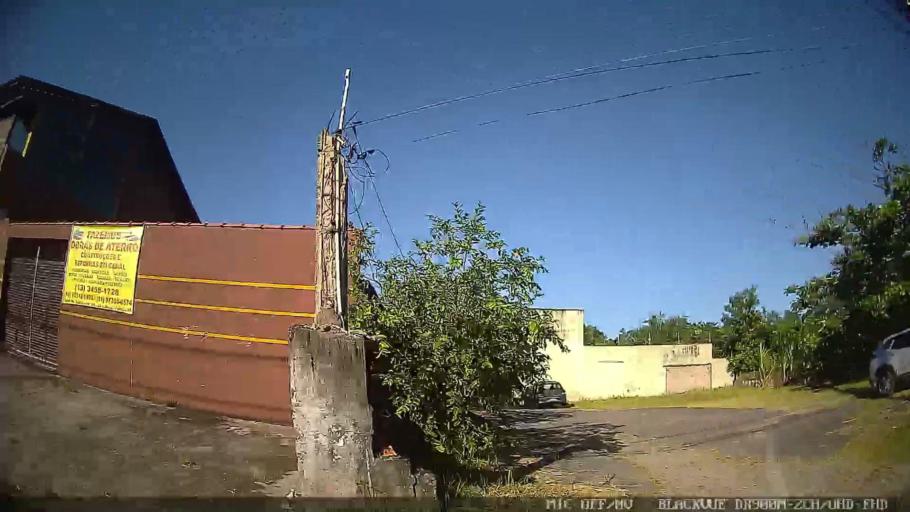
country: BR
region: Sao Paulo
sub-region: Peruibe
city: Peruibe
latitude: -24.2766
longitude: -46.9501
